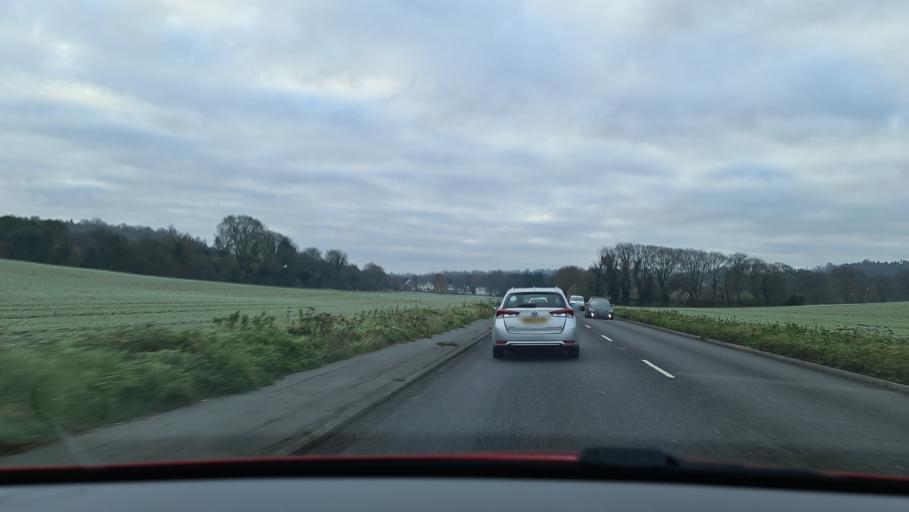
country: GB
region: England
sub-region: Buckinghamshire
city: High Wycombe
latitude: 51.6498
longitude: -0.7979
